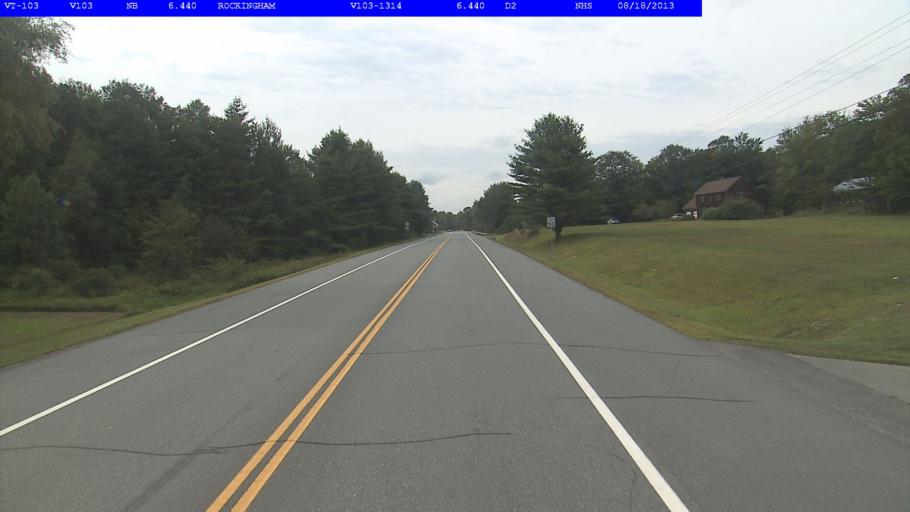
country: US
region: Vermont
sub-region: Windsor County
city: Chester
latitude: 43.2320
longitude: -72.5486
